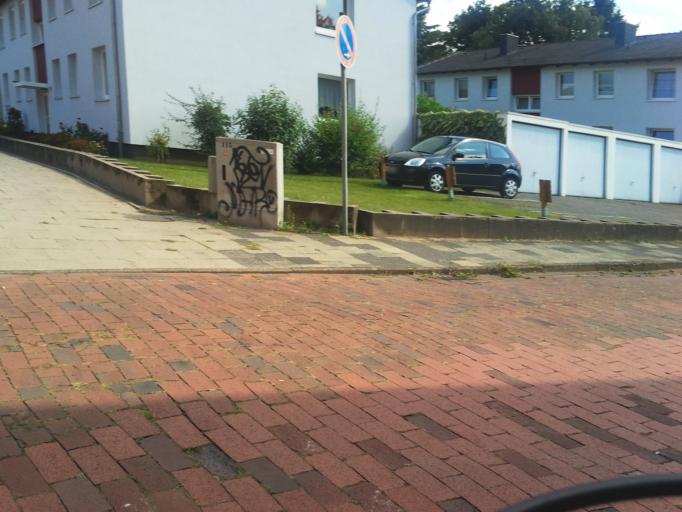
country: DE
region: Lower Saxony
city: Nienburg
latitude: 52.6366
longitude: 9.2108
